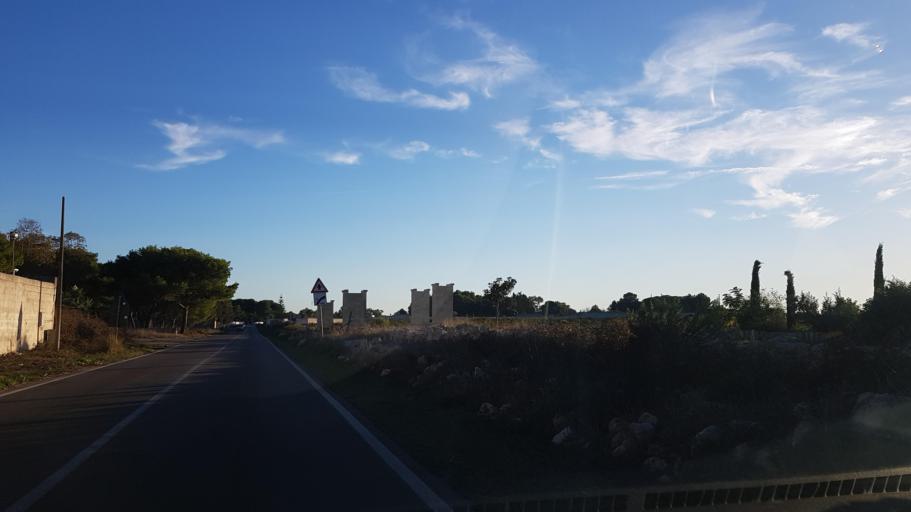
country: IT
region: Apulia
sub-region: Provincia di Lecce
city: Giorgilorio
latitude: 40.4026
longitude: 18.1967
